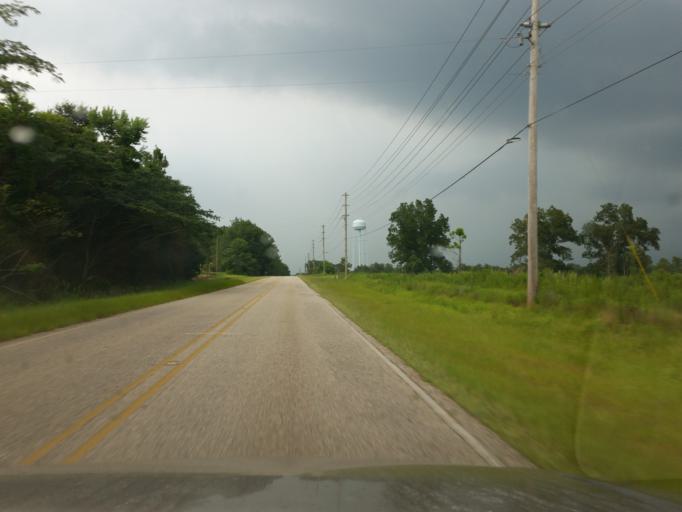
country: US
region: Alabama
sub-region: Baldwin County
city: Robertsdale
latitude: 30.5515
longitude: -87.5816
